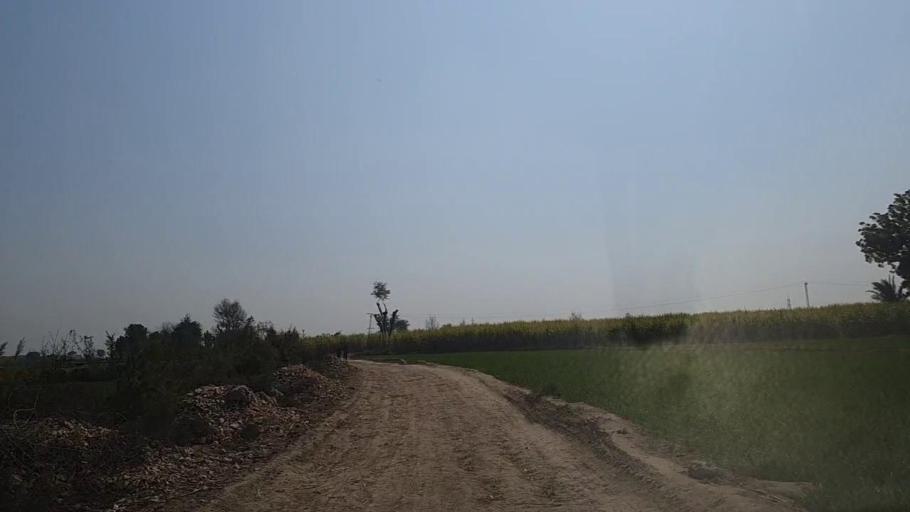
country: PK
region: Sindh
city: Moro
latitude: 26.6960
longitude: 67.9281
